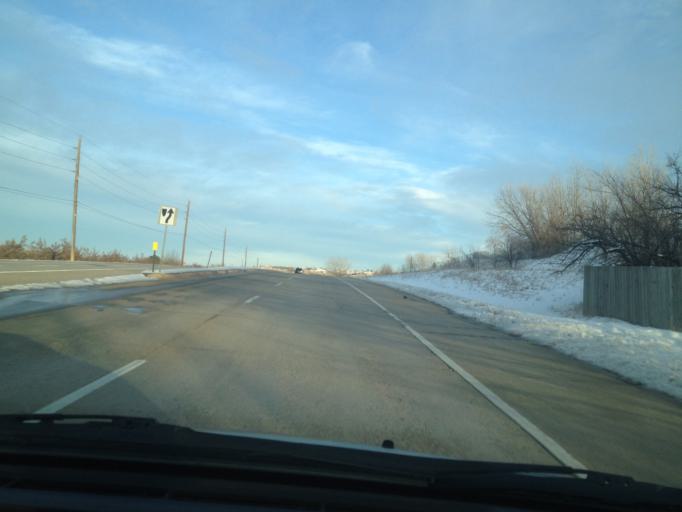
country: US
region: Colorado
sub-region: Boulder County
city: Superior
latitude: 39.9861
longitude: -105.2019
